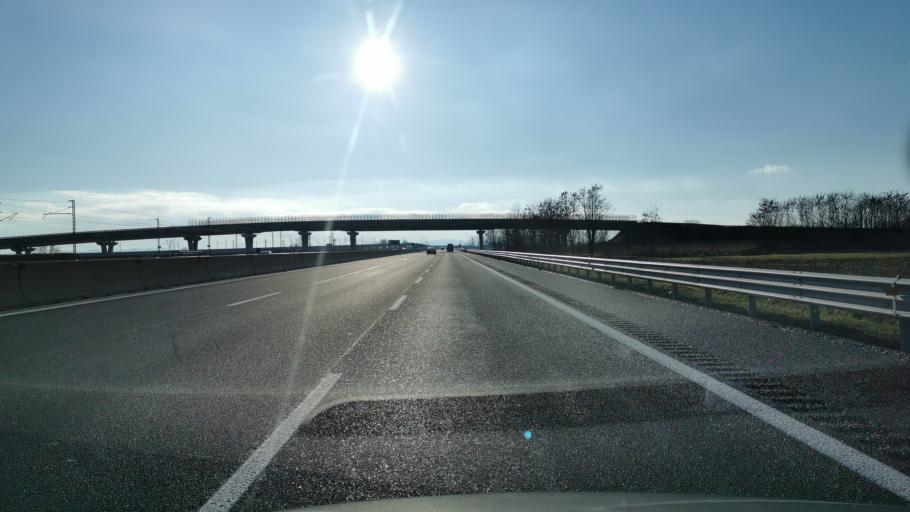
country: IT
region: Piedmont
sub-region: Provincia di Vercelli
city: Livorno Ferraris
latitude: 45.3103
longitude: 8.0607
